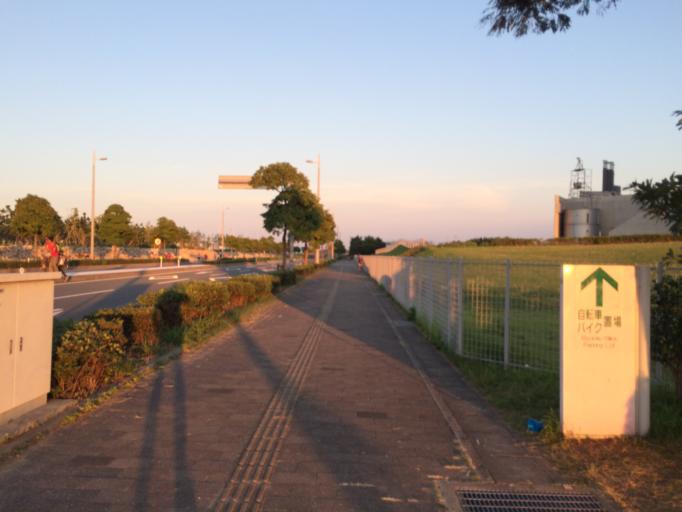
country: JP
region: Yamaguchi
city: Ogori-shimogo
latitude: 34.0096
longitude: 131.3726
